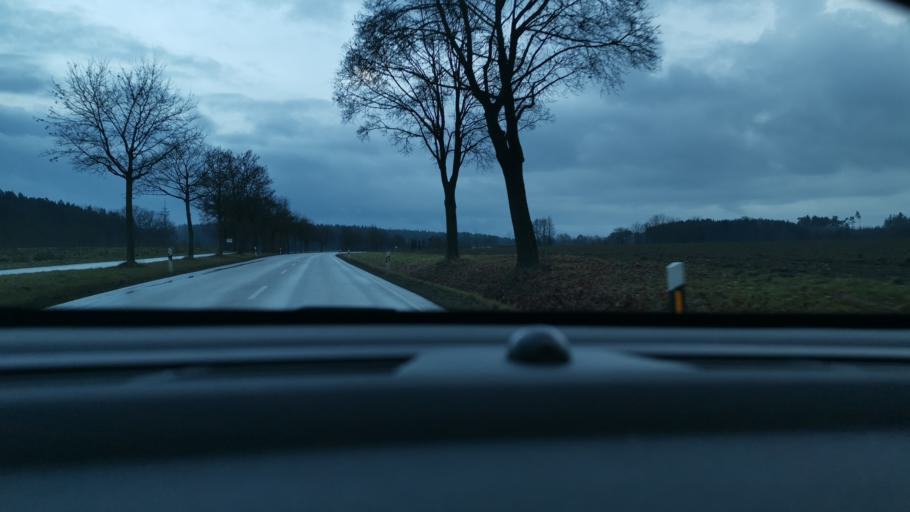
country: DE
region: Bavaria
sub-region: Swabia
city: Petersdorf
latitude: 48.5037
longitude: 11.0159
